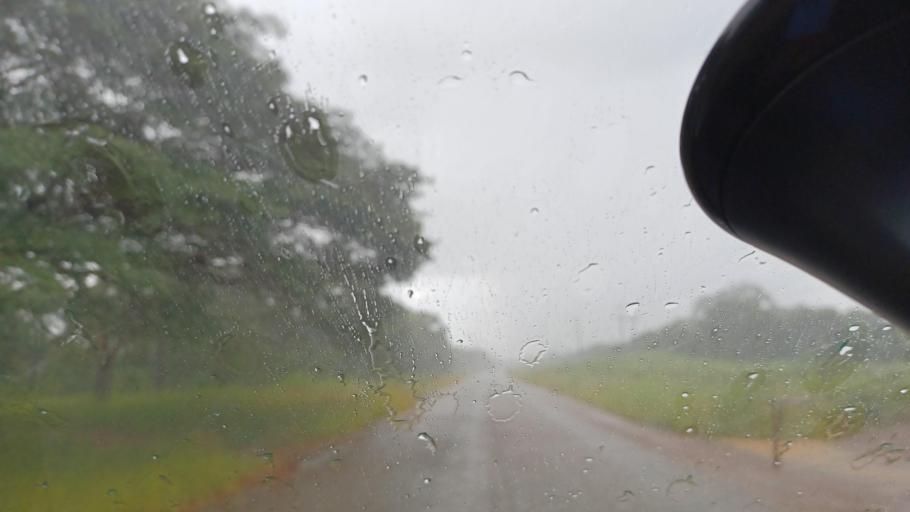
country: ZM
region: North-Western
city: Kasempa
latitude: -13.0904
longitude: 25.9473
